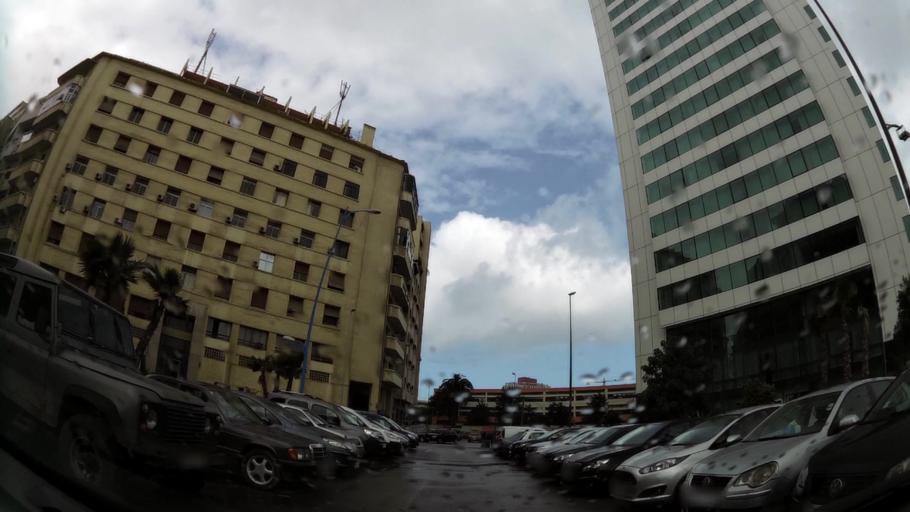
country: MA
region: Grand Casablanca
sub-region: Casablanca
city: Casablanca
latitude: 33.5945
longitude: -7.6001
